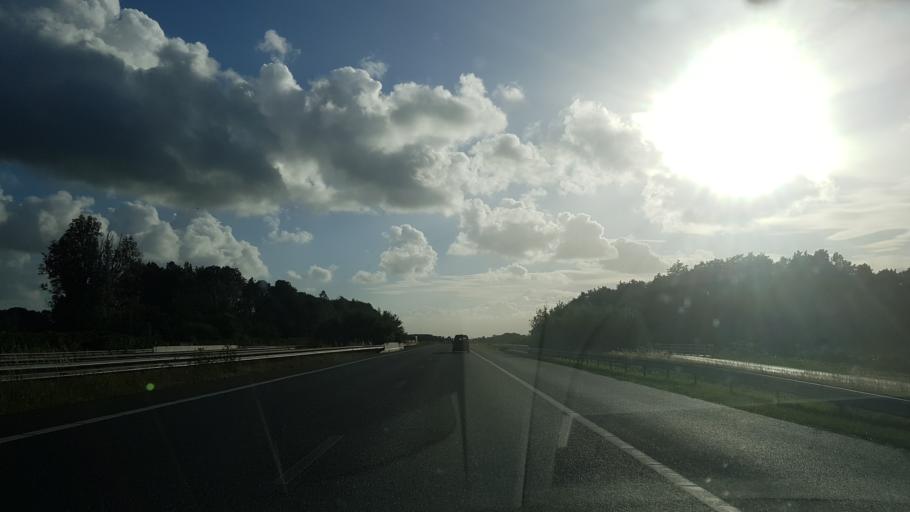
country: NL
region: Groningen
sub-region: Gemeente Leek
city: Leek
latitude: 53.1945
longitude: 6.4173
